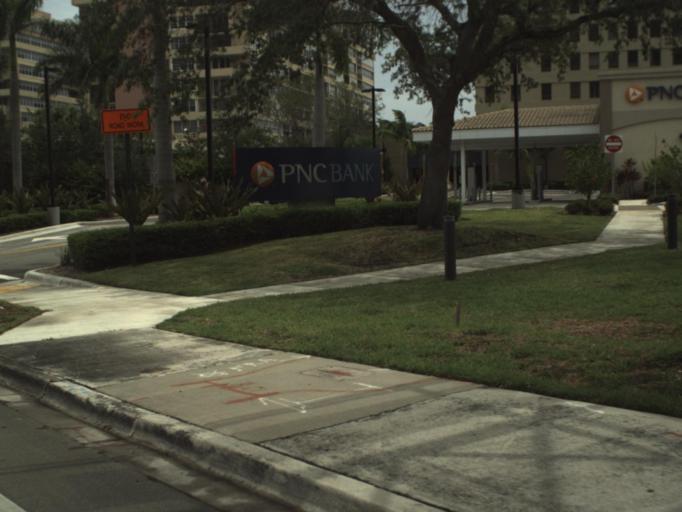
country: US
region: Florida
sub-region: Broward County
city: Sunrise
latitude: 26.1380
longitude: -80.1206
